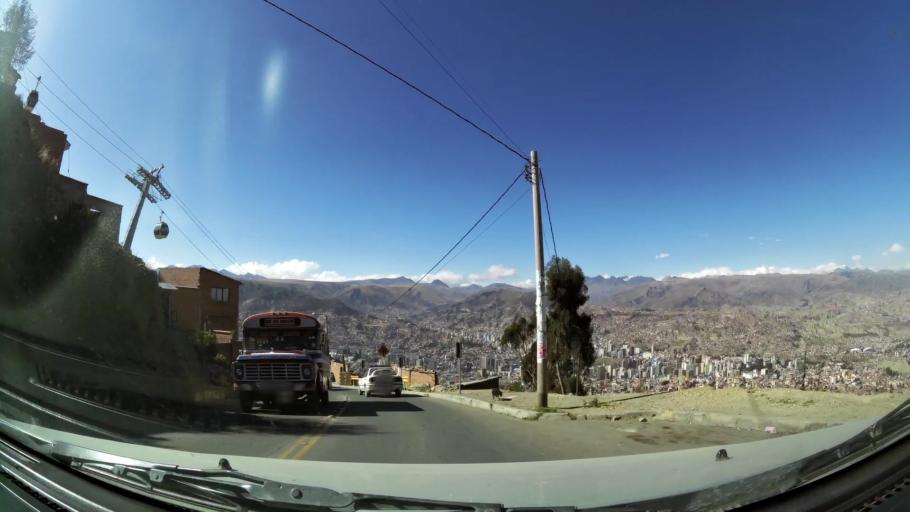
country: BO
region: La Paz
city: La Paz
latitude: -16.5171
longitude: -68.1465
